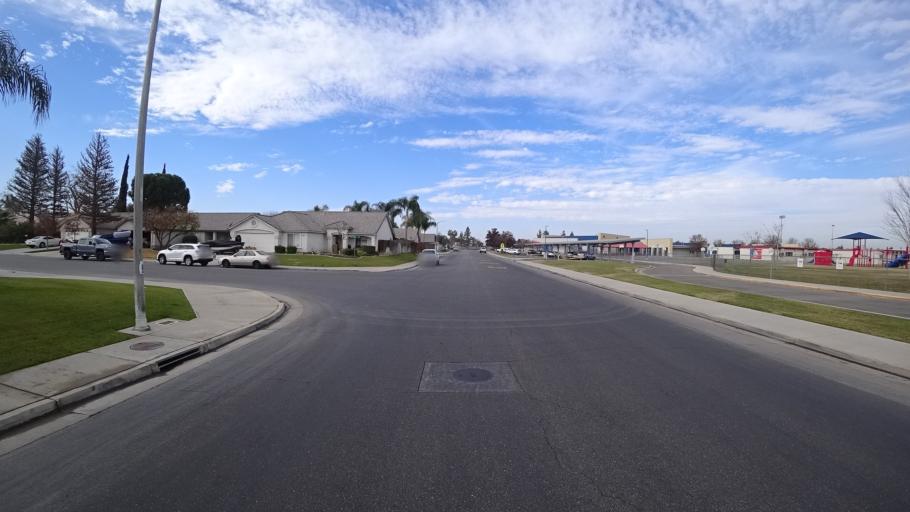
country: US
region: California
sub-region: Kern County
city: Rosedale
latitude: 35.4002
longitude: -119.1339
